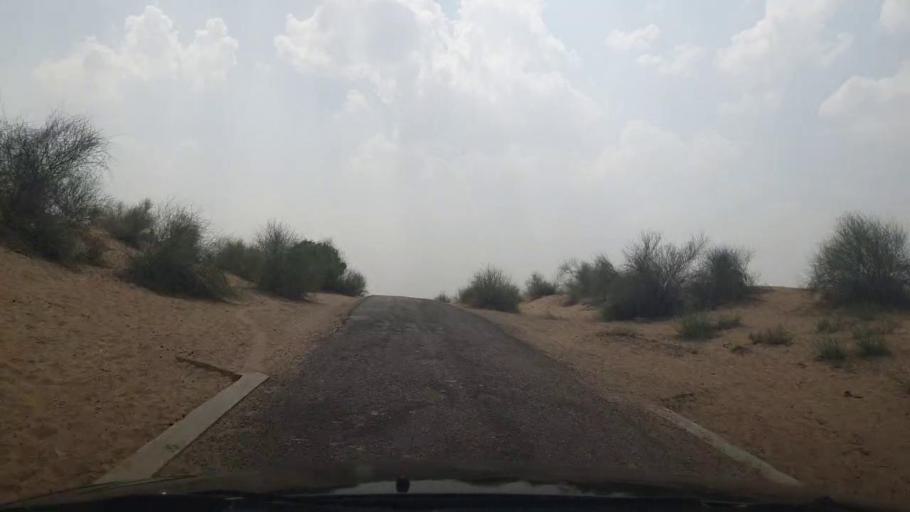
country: PK
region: Sindh
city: Islamkot
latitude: 25.0008
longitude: 70.4999
